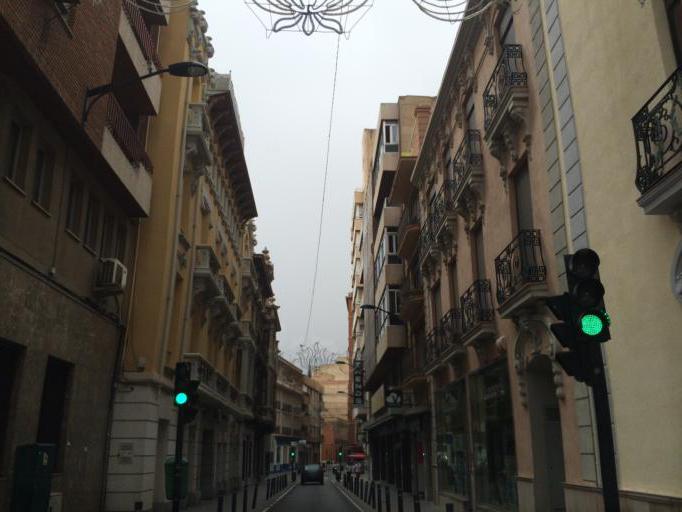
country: ES
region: Castille-La Mancha
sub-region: Provincia de Albacete
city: Albacete
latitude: 38.9959
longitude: -1.8568
